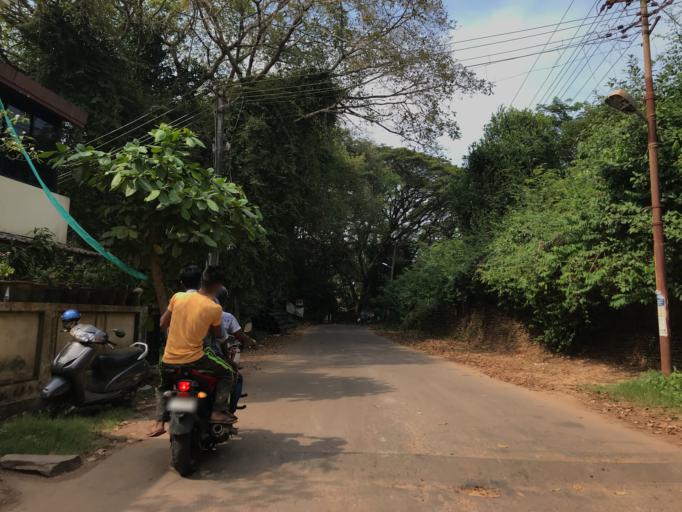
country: IN
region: Karnataka
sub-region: Dakshina Kannada
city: Ullal
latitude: 12.8462
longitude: 74.8527
